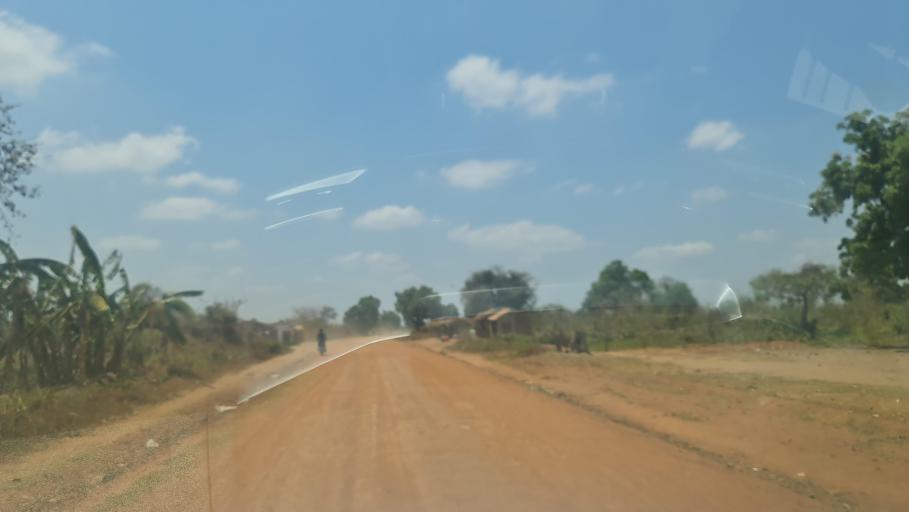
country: MW
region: Southern Region
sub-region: Nsanje District
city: Nsanje
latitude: -17.3233
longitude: 35.7070
